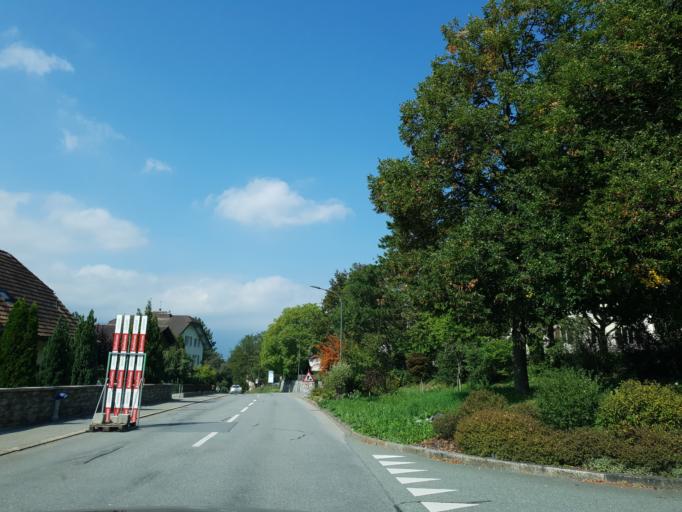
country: LI
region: Vaduz
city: Vaduz
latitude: 47.1497
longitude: 9.5150
